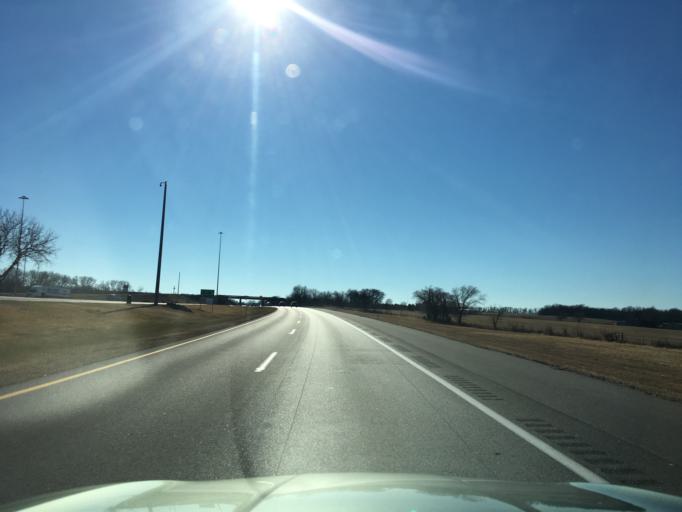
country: US
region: Kansas
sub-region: Sumner County
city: Belle Plaine
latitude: 37.3668
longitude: -97.3235
